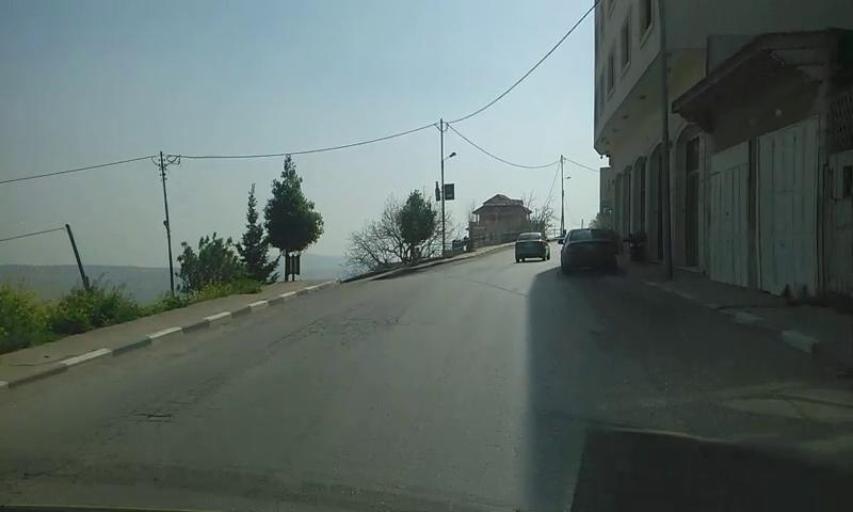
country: PS
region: West Bank
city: At Taybah
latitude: 31.9555
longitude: 35.2995
